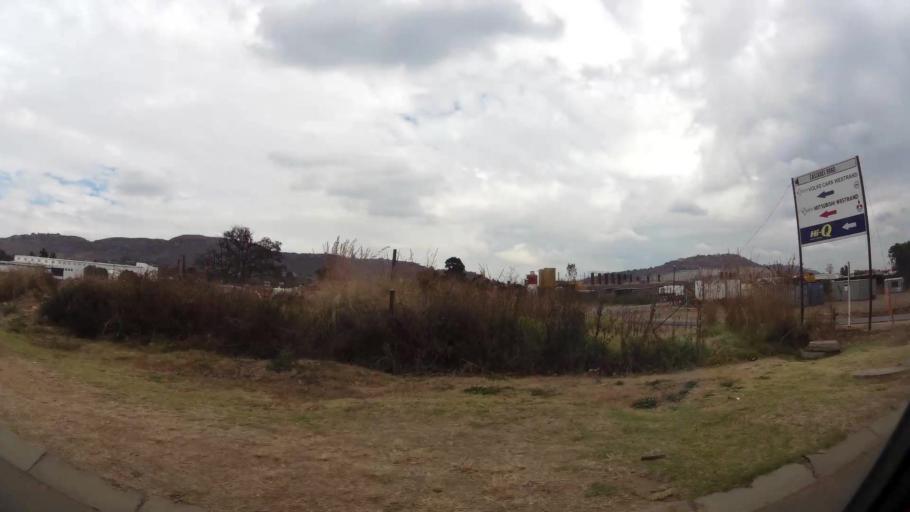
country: ZA
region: Gauteng
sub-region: City of Johannesburg Metropolitan Municipality
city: Roodepoort
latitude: -26.1119
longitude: 27.8922
